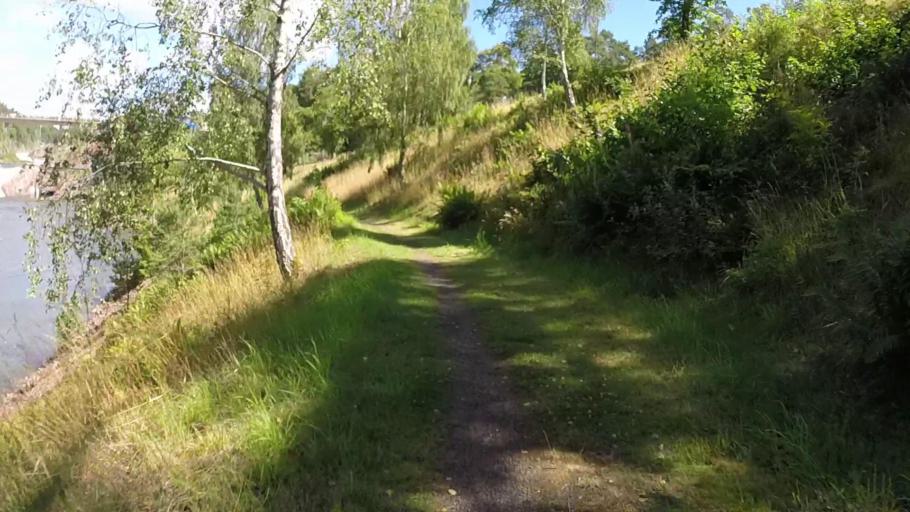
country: SE
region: Vaestra Goetaland
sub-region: Trollhattan
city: Trollhattan
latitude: 58.2778
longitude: 12.2765
